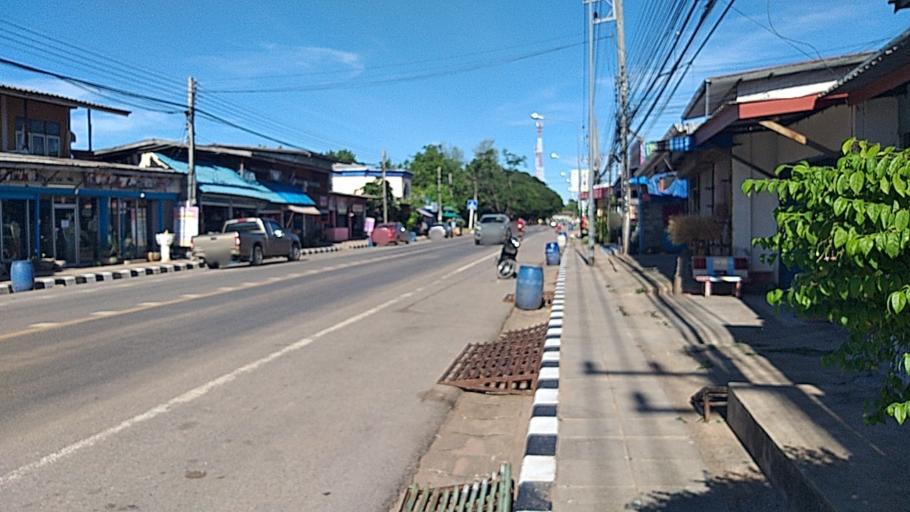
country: TH
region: Chaiyaphum
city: Ban Thaen
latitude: 16.4082
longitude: 102.3497
